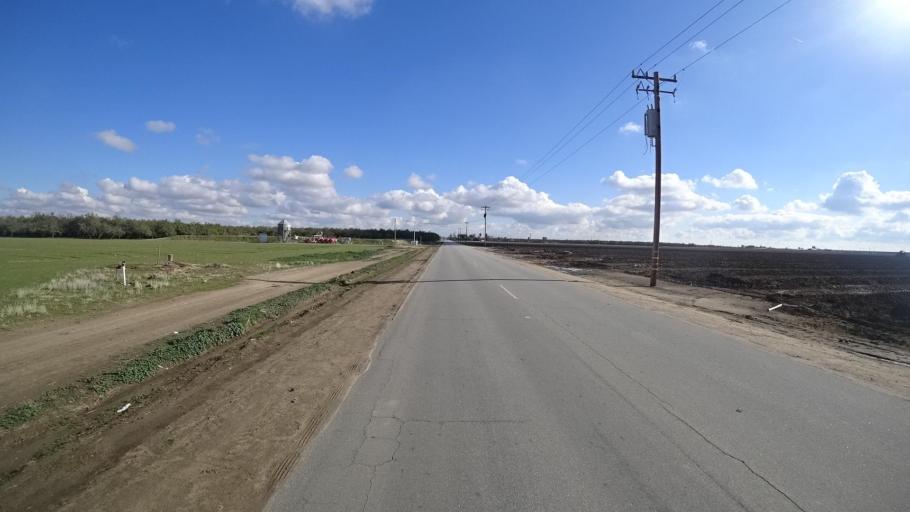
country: US
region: California
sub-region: Kern County
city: McFarland
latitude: 35.6744
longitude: -119.2642
